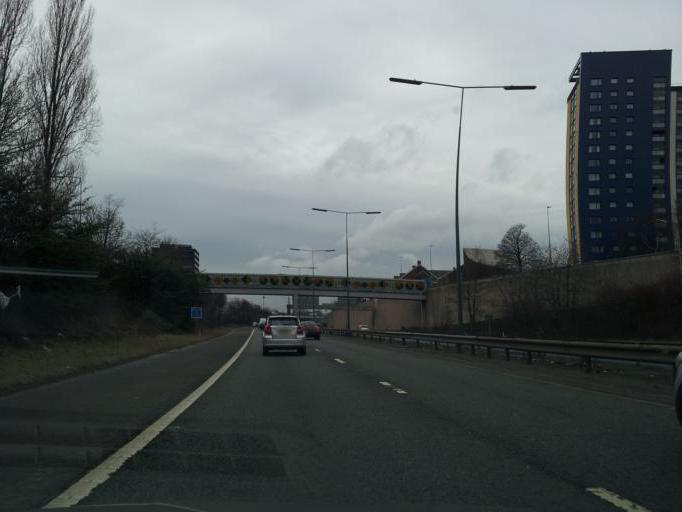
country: GB
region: England
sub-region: City and Borough of Salford
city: Eccles
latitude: 53.4860
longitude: -2.3328
